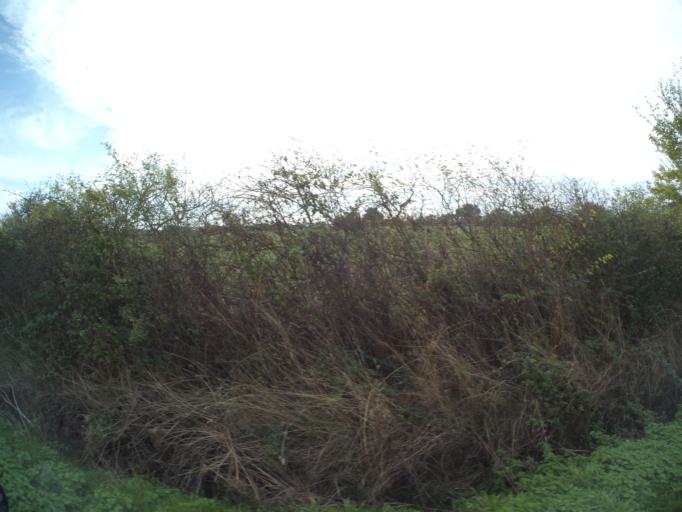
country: FR
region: Pays de la Loire
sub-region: Departement de Maine-et-Loire
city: Vihiers
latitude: 47.2061
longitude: -0.5596
